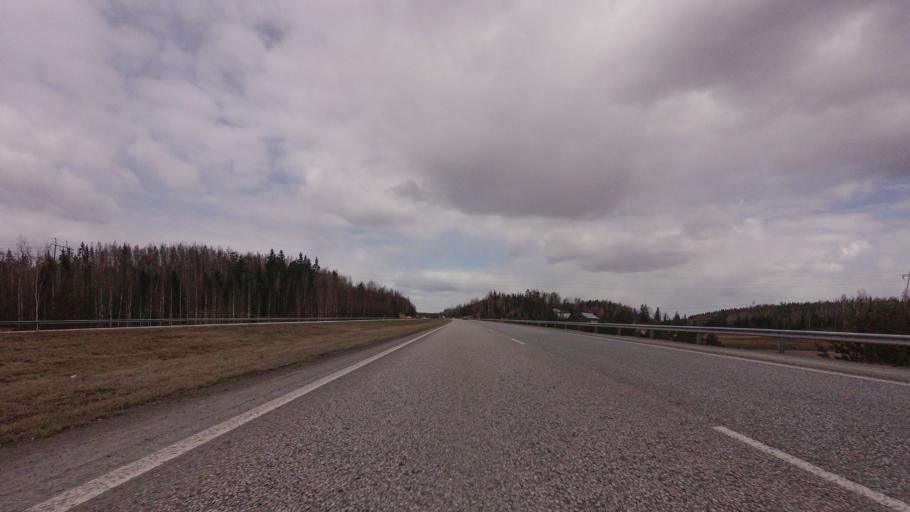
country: FI
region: Uusimaa
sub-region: Helsinki
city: Nurmijaervi
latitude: 60.3809
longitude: 24.8150
